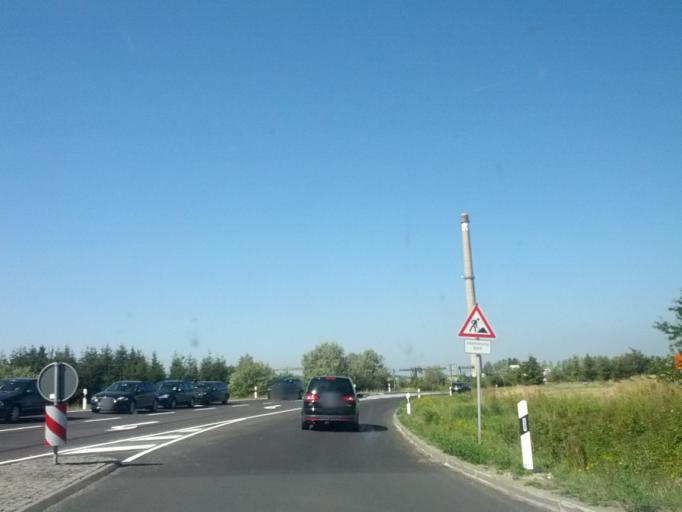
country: DE
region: Mecklenburg-Vorpommern
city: Sagard
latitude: 54.4927
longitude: 13.5787
